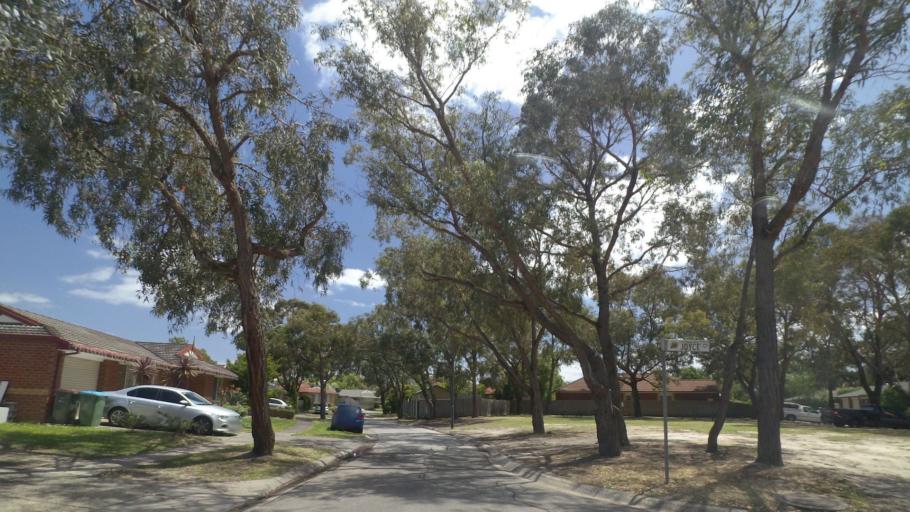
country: AU
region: Victoria
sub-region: Maroondah
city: Bayswater North
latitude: -37.8242
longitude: 145.3031
